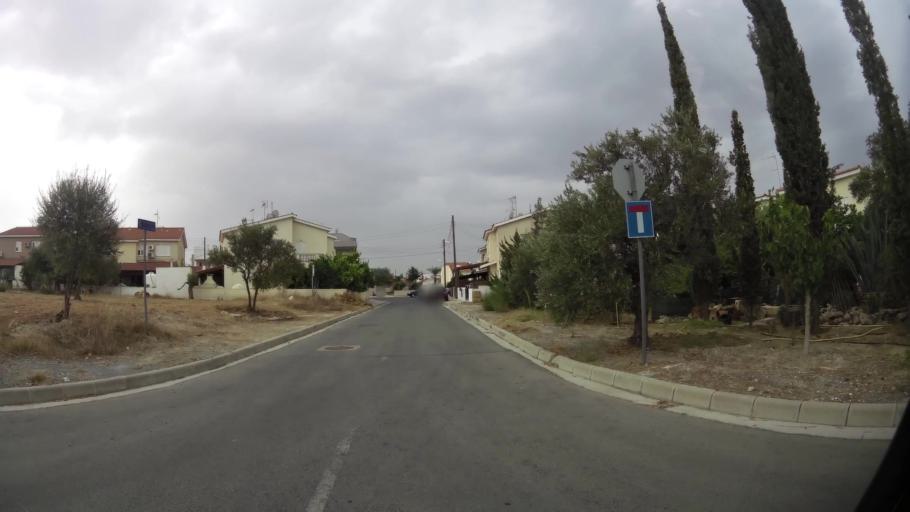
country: CY
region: Lefkosia
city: Geri
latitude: 35.1007
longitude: 33.3894
